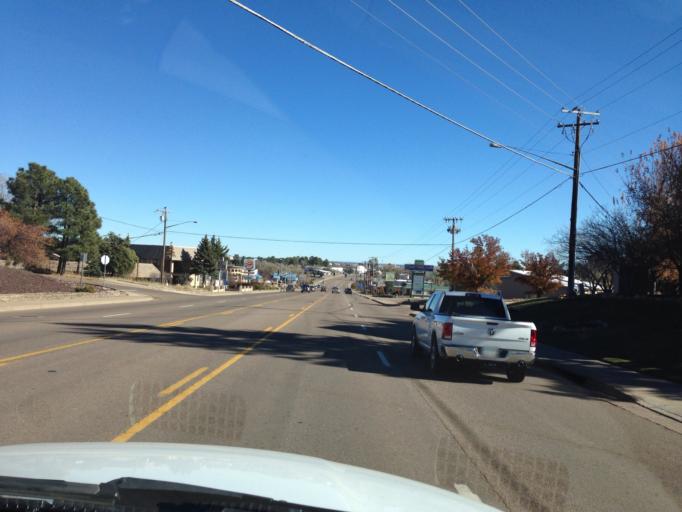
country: US
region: Arizona
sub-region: Navajo County
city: Show Low
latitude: 34.2495
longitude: -110.0443
